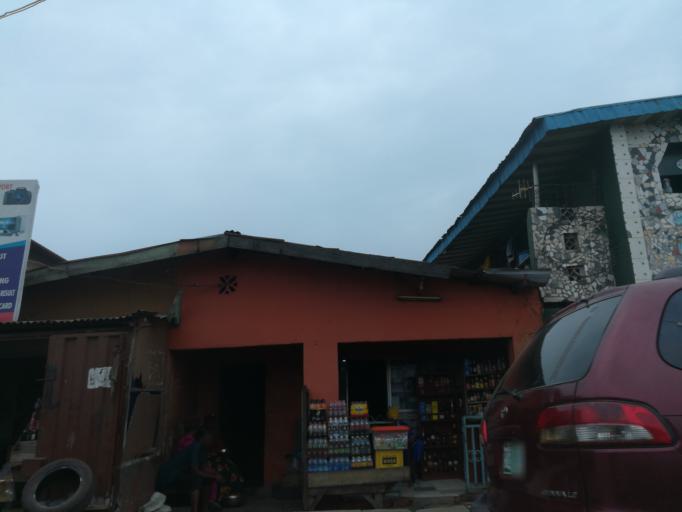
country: NG
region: Lagos
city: Makoko
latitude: 6.5001
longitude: 3.3891
